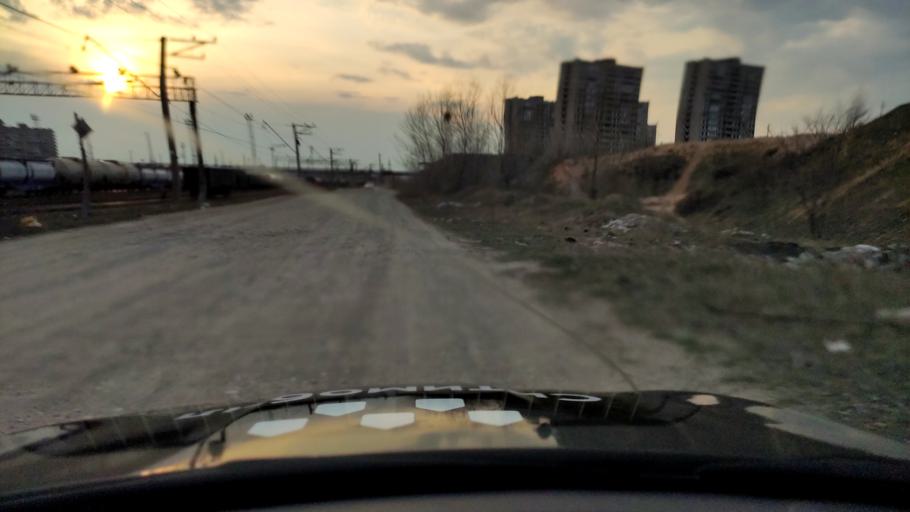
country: RU
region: Samara
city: Zhigulevsk
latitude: 53.4777
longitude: 49.5307
